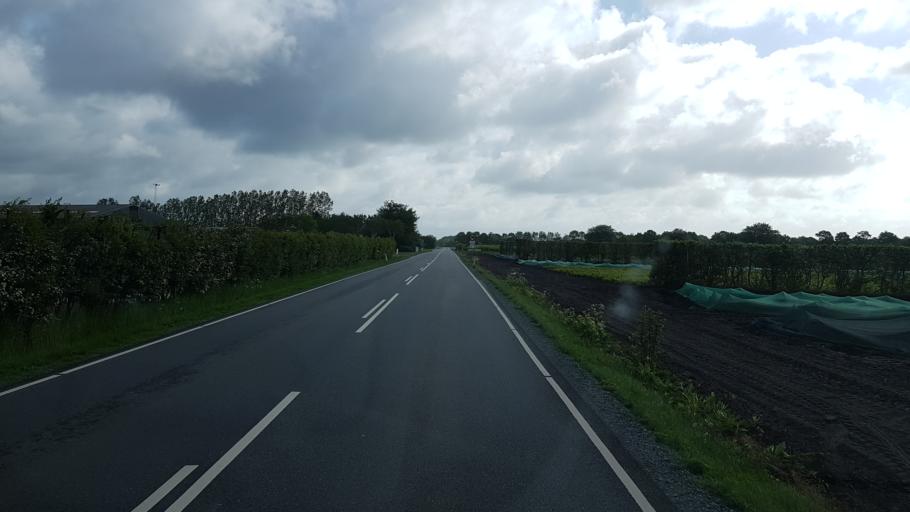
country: DK
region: South Denmark
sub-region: Vejen Kommune
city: Vejen
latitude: 55.4535
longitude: 9.1549
